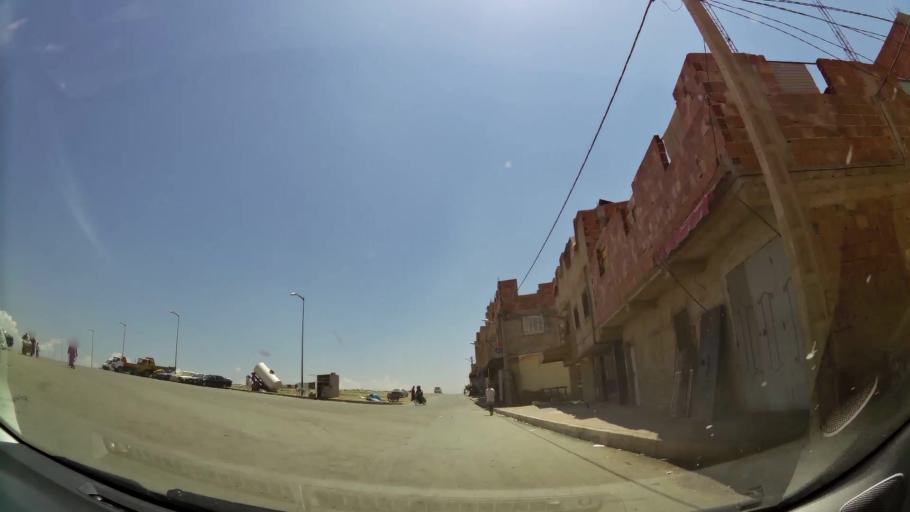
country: MA
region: Oriental
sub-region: Oujda-Angad
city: Oujda
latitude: 34.6922
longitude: -1.9475
